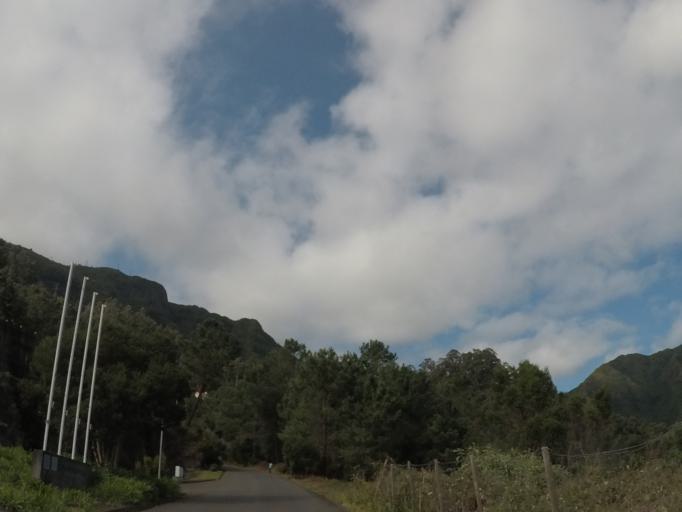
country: PT
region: Madeira
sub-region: Sao Vicente
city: Sao Vicente
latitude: 32.7801
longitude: -17.0464
